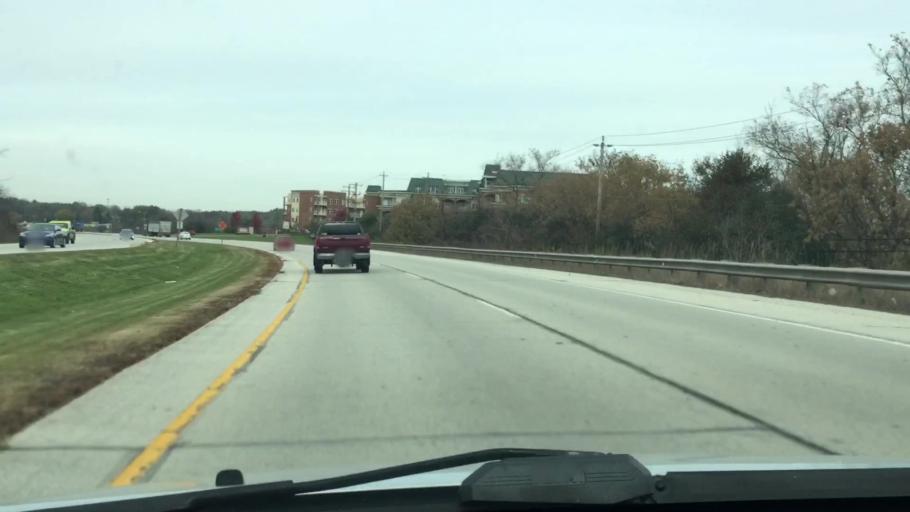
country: US
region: Wisconsin
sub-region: Milwaukee County
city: Franklin
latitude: 42.9096
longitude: -88.0395
